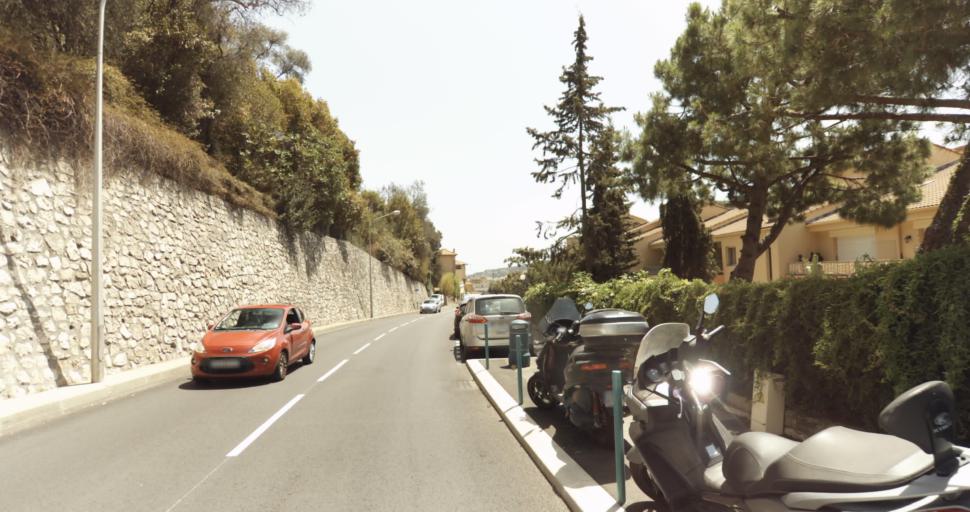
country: FR
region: Provence-Alpes-Cote d'Azur
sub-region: Departement des Alpes-Maritimes
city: Roquebrune-Cap-Martin
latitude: 43.7700
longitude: 7.4798
